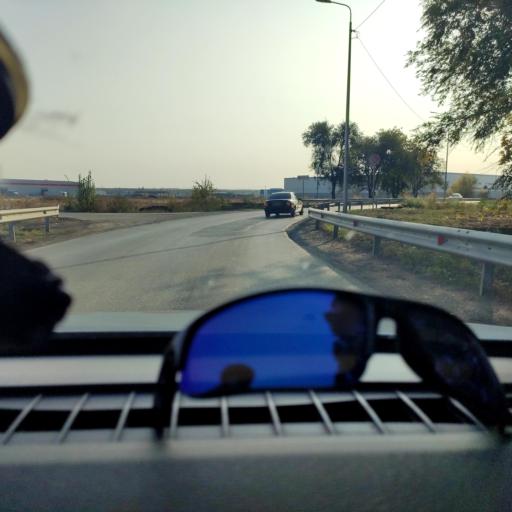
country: RU
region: Samara
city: Samara
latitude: 53.0981
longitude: 50.1406
